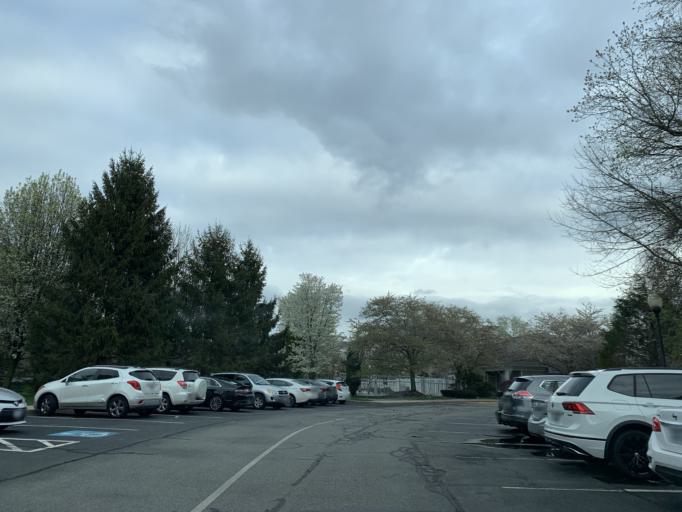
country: US
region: Rhode Island
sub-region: Kent County
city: West Warwick
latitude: 41.6745
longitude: -71.5047
